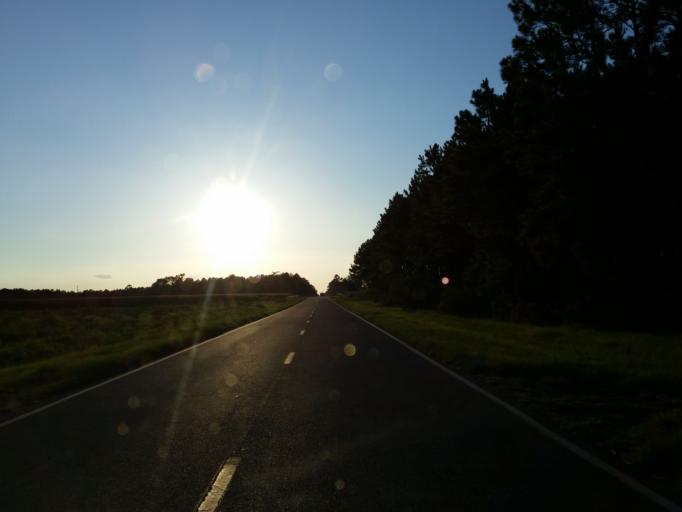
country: US
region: Georgia
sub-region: Lanier County
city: Lakeland
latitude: 31.1647
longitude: -83.0910
